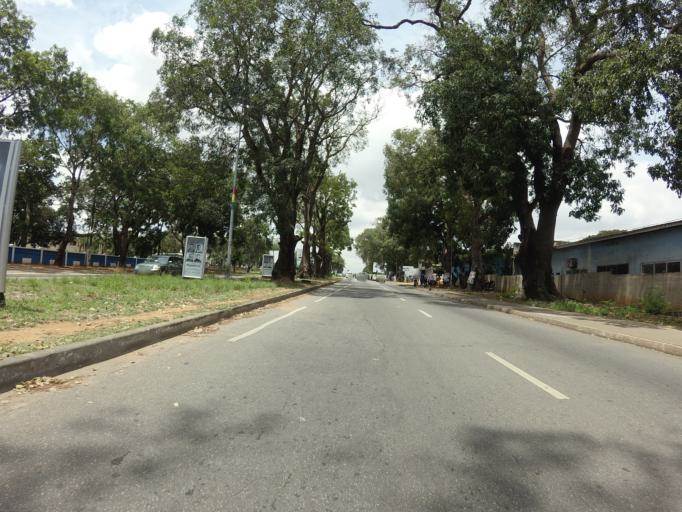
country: GH
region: Greater Accra
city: Accra
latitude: 5.5607
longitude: -0.2059
